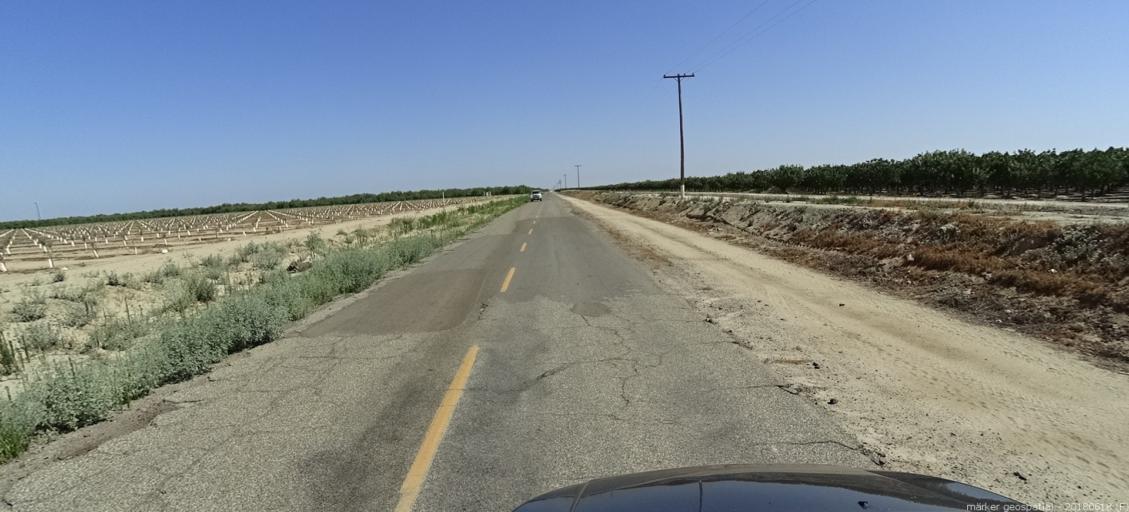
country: US
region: California
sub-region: Fresno County
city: Mendota
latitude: 36.8389
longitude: -120.2551
